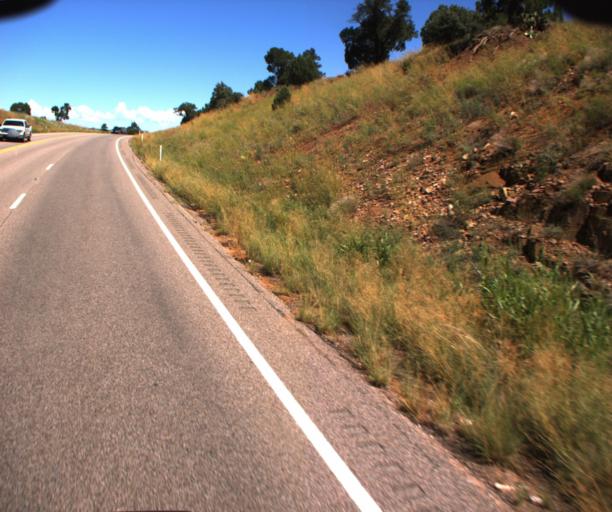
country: US
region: Arizona
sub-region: Gila County
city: San Carlos
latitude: 33.6581
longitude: -110.5714
